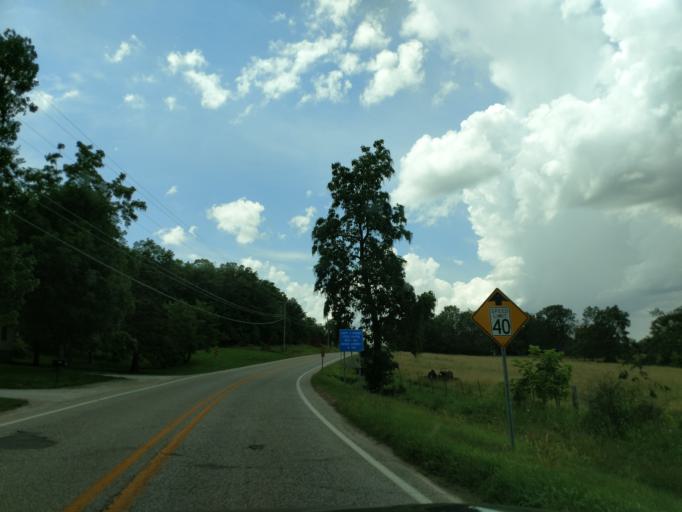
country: US
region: Arkansas
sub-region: Boone County
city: Harrison
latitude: 36.2478
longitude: -93.2127
